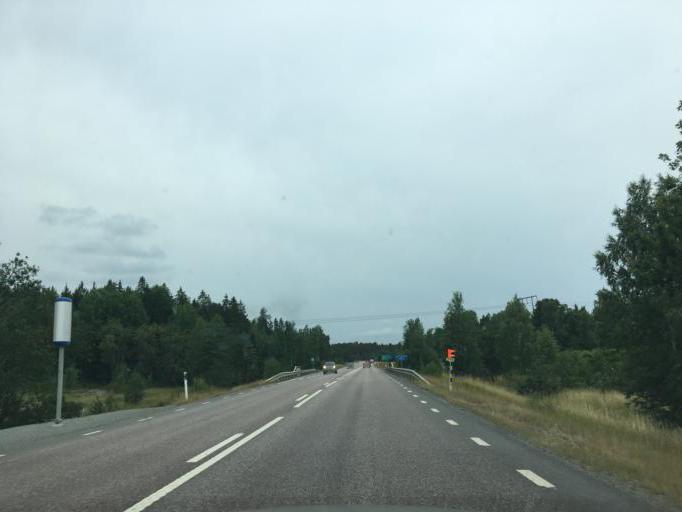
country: SE
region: Soedermanland
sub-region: Strangnas Kommun
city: Strangnas
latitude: 59.3833
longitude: 16.9862
